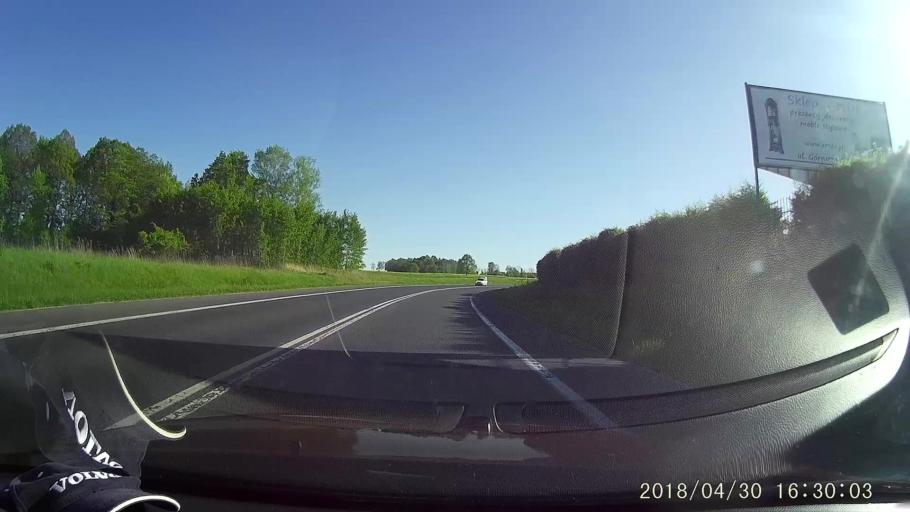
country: PL
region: Lower Silesian Voivodeship
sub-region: Powiat zgorzelecki
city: Zgorzelec
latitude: 51.1292
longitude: 15.0216
